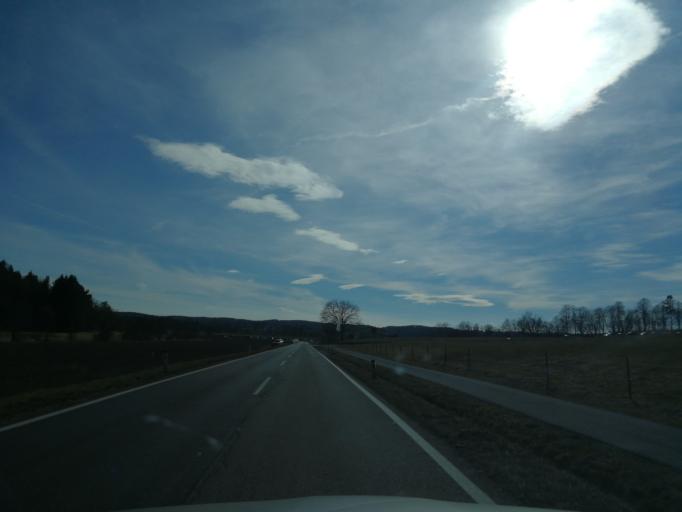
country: AT
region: Styria
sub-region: Politischer Bezirk Graz-Umgebung
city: Unterpremstatten
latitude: 46.9492
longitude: 15.3834
